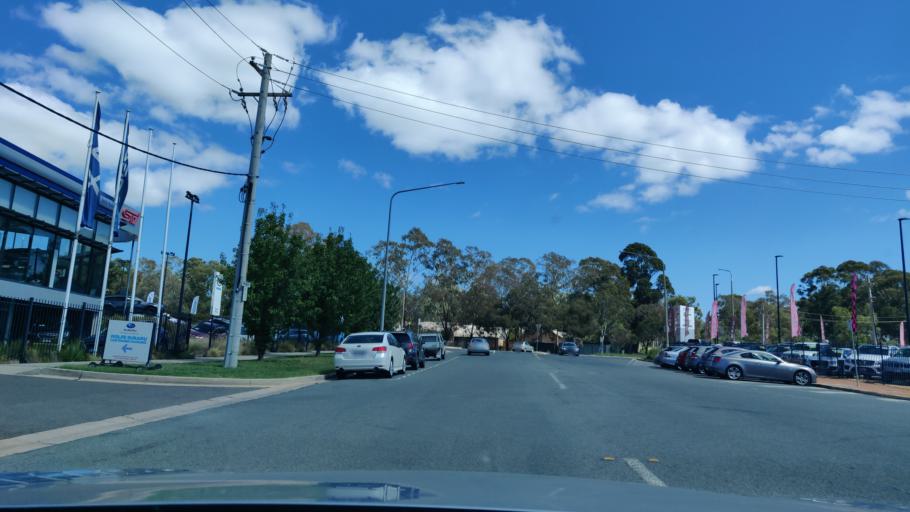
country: AU
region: Australian Capital Territory
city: Forrest
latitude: -35.3557
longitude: 149.0878
